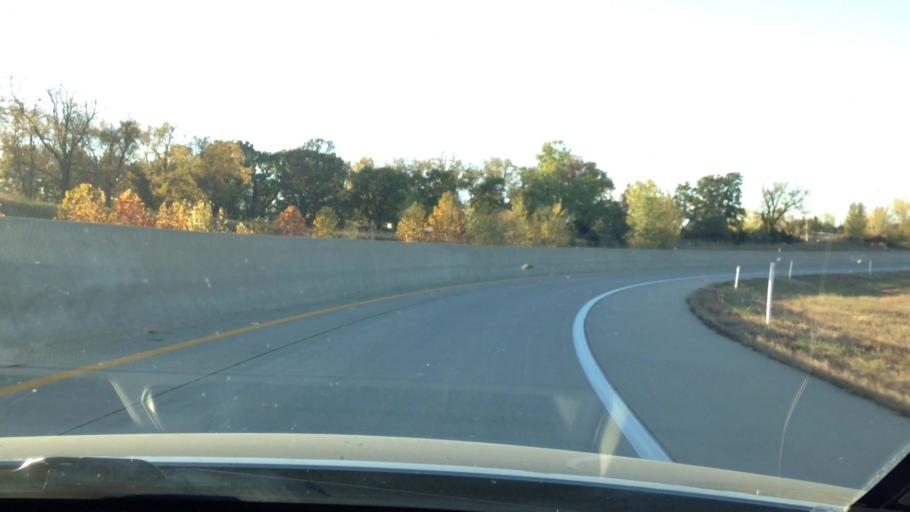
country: US
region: Kansas
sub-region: Leavenworth County
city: Basehor
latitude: 39.1142
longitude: -94.8957
